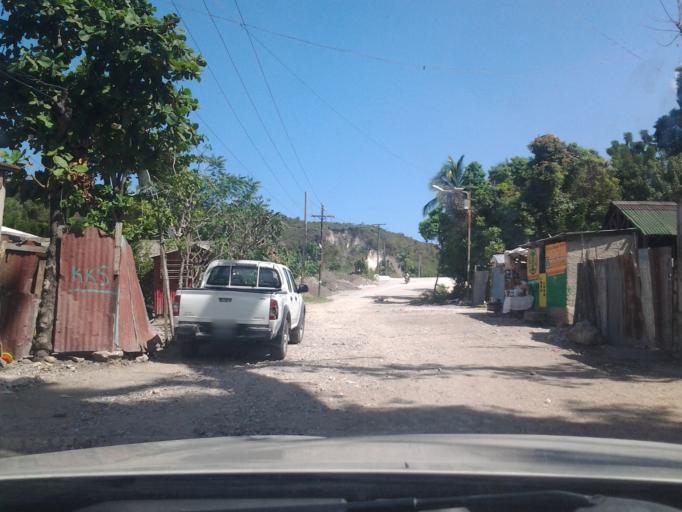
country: HT
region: Ouest
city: Tigwav
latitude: 18.4404
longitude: -72.8461
